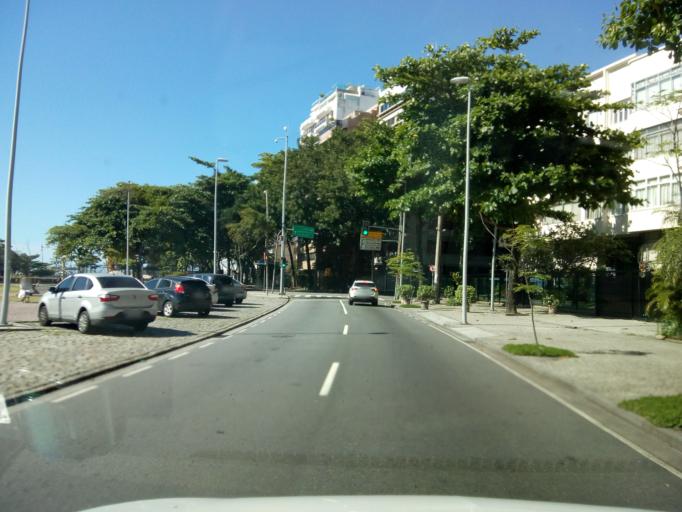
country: BR
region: Rio de Janeiro
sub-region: Rio De Janeiro
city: Rio de Janeiro
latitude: -22.9841
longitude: -43.2159
